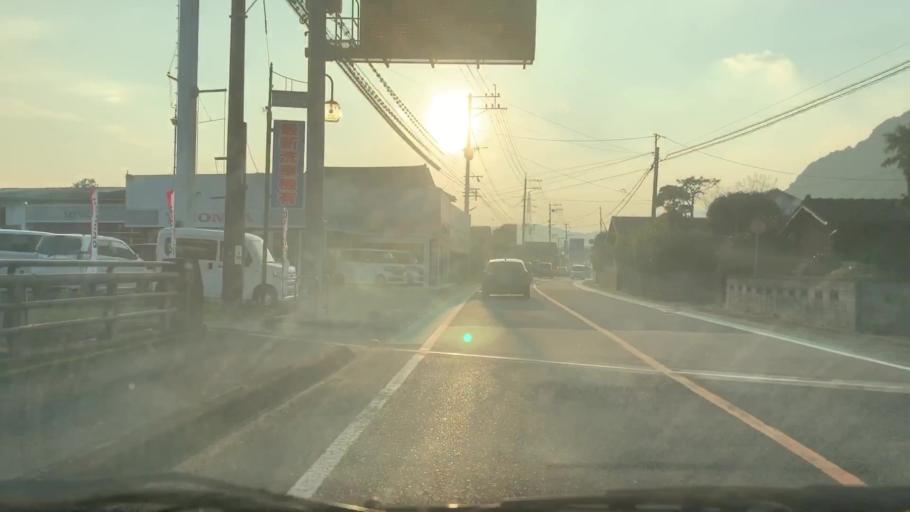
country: JP
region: Saga Prefecture
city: Takeocho-takeo
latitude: 33.2600
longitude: 130.0843
